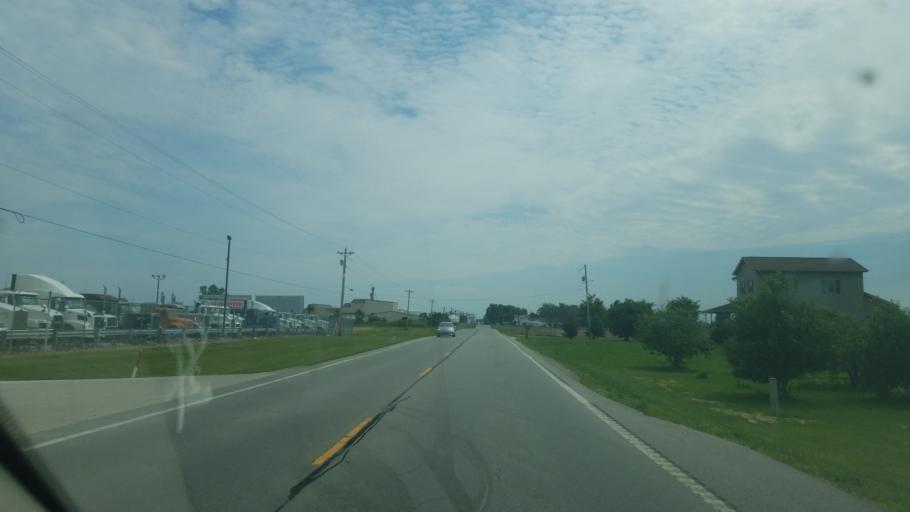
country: US
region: Ohio
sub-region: Seneca County
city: Fostoria
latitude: 41.1378
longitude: -83.4558
